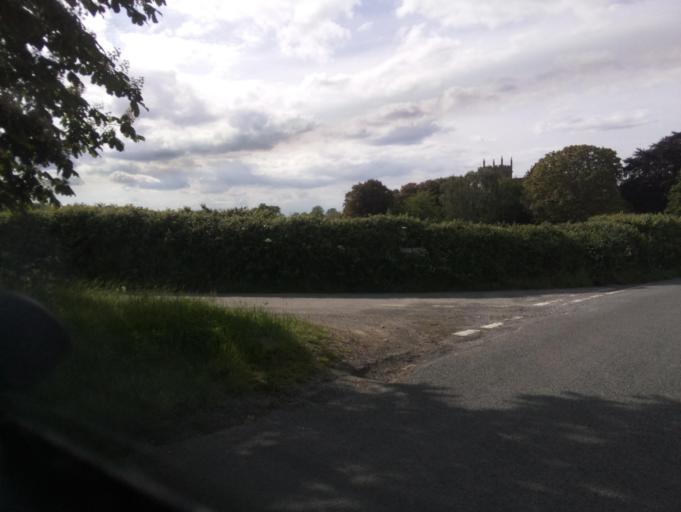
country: GB
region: England
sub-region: Gloucestershire
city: Chipping Campden
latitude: 52.0626
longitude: -1.8133
